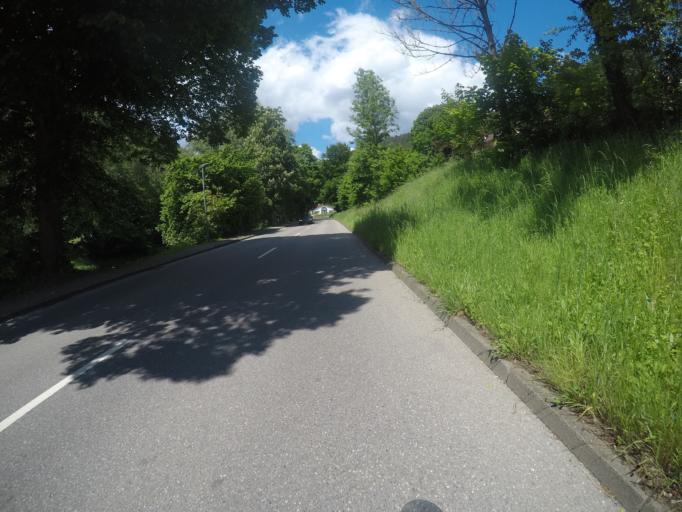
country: DE
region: Baden-Wuerttemberg
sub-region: Karlsruhe Region
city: Bad Liebenzell
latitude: 48.7795
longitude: 8.7333
